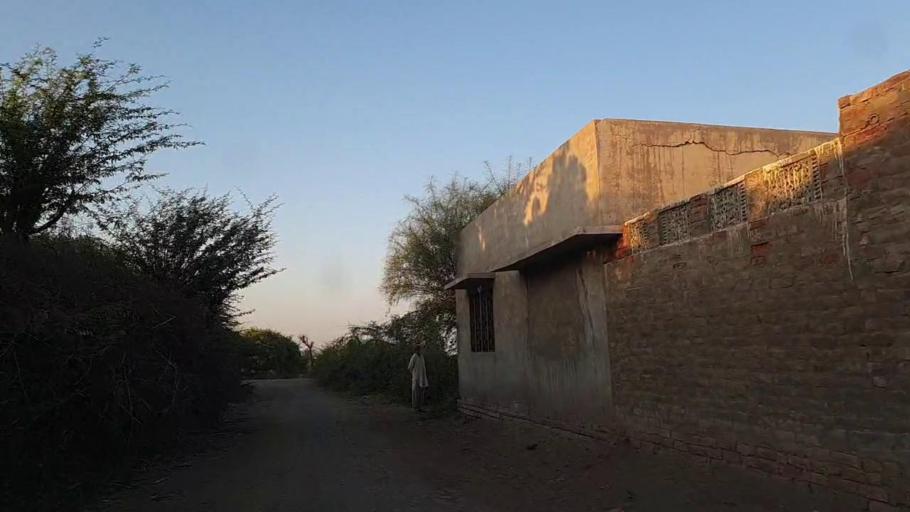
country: PK
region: Sindh
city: Samaro
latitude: 25.3028
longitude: 69.3970
